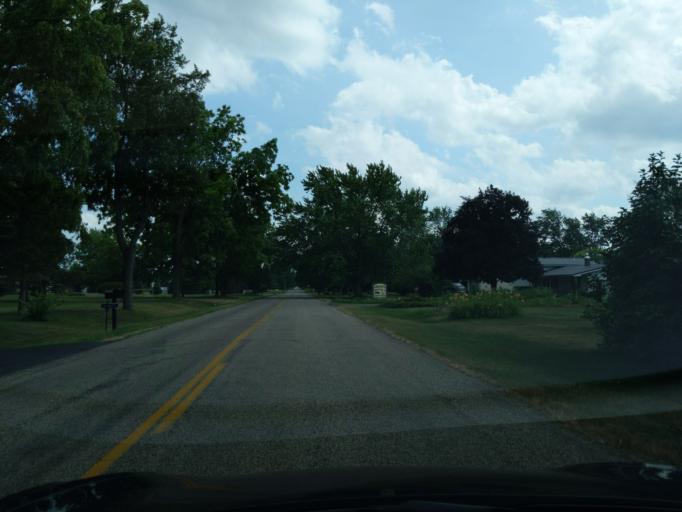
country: US
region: Michigan
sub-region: Eaton County
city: Eaton Rapids
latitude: 42.5139
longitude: -84.6014
